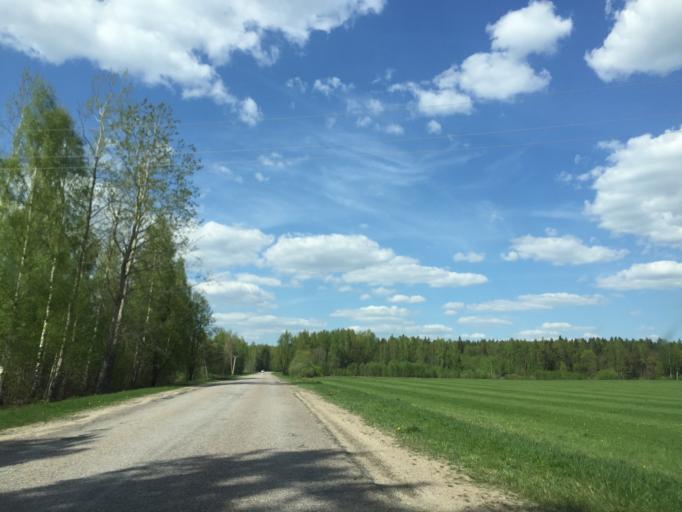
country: LV
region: Limbazu Rajons
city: Limbazi
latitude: 57.4011
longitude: 24.6911
